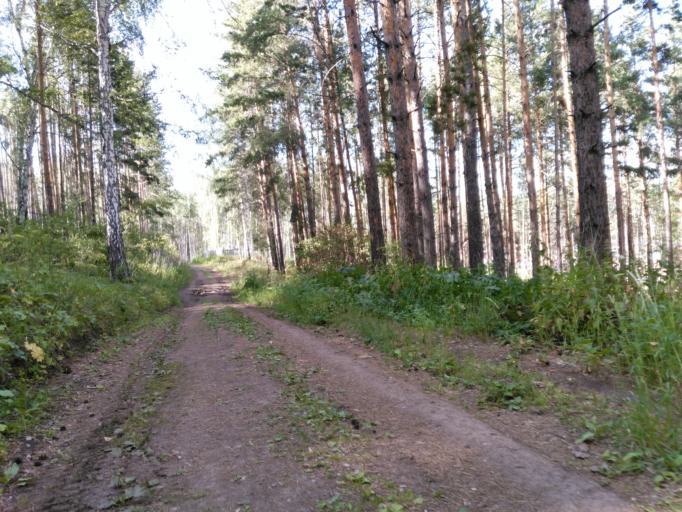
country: RU
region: Bashkortostan
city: Uchaly
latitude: 54.3273
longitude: 59.3606
